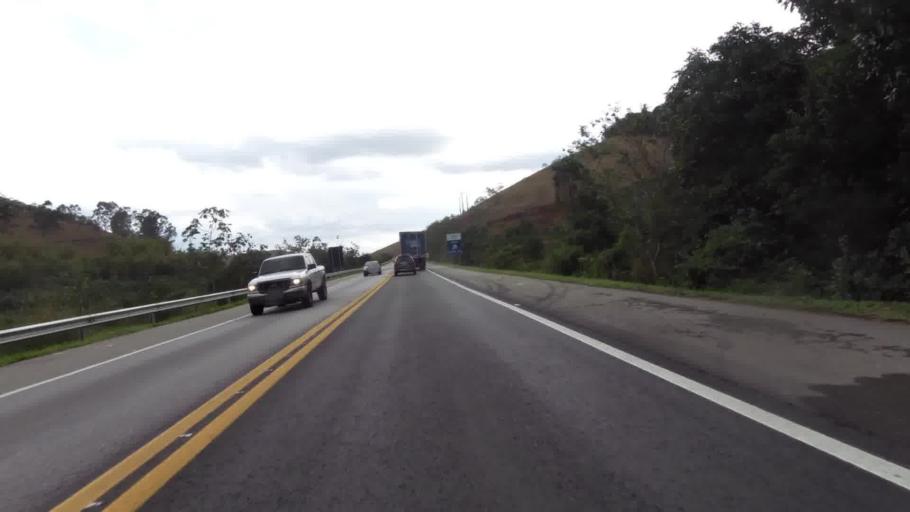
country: BR
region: Rio de Janeiro
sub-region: Rio Das Ostras
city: Rio das Ostras
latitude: -22.4611
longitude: -42.0638
